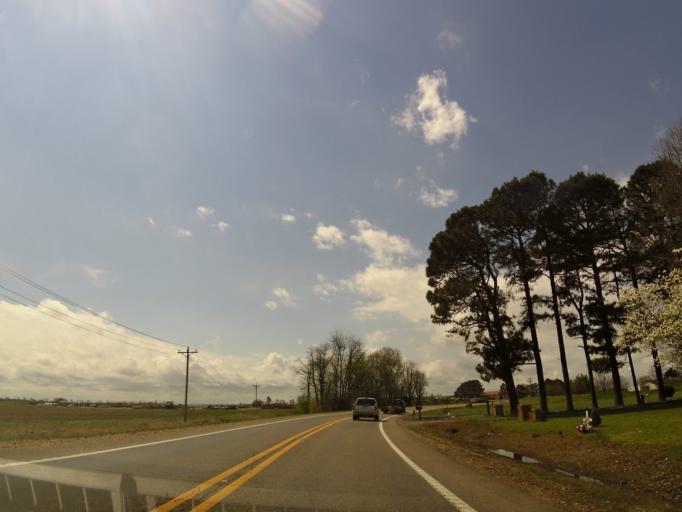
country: US
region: Arkansas
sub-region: Clay County
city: Corning
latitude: 36.3803
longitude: -90.5200
